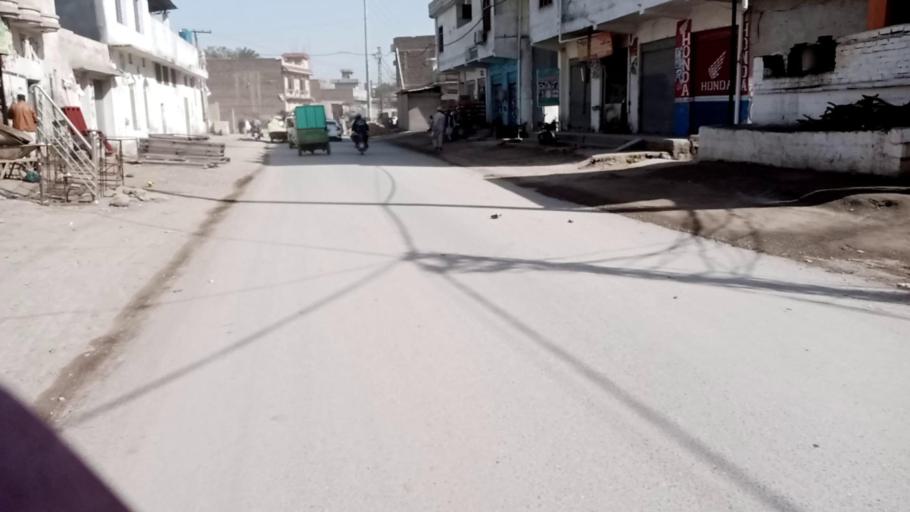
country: PK
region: Khyber Pakhtunkhwa
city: Peshawar
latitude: 34.0060
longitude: 71.6410
